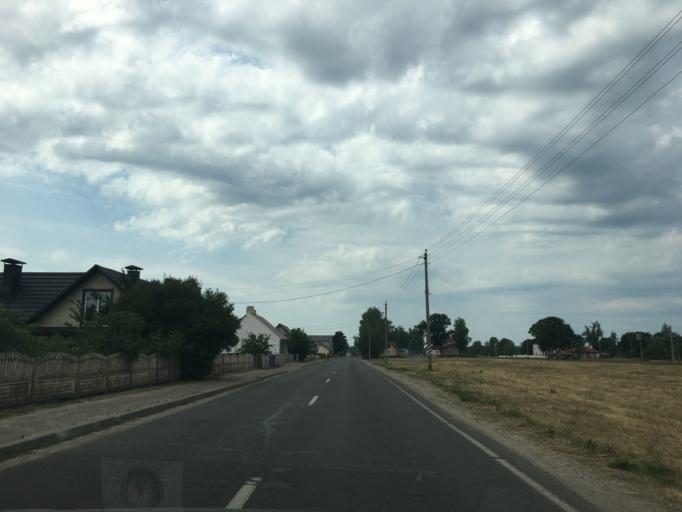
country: LT
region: Alytaus apskritis
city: Druskininkai
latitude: 53.8887
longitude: 24.1383
